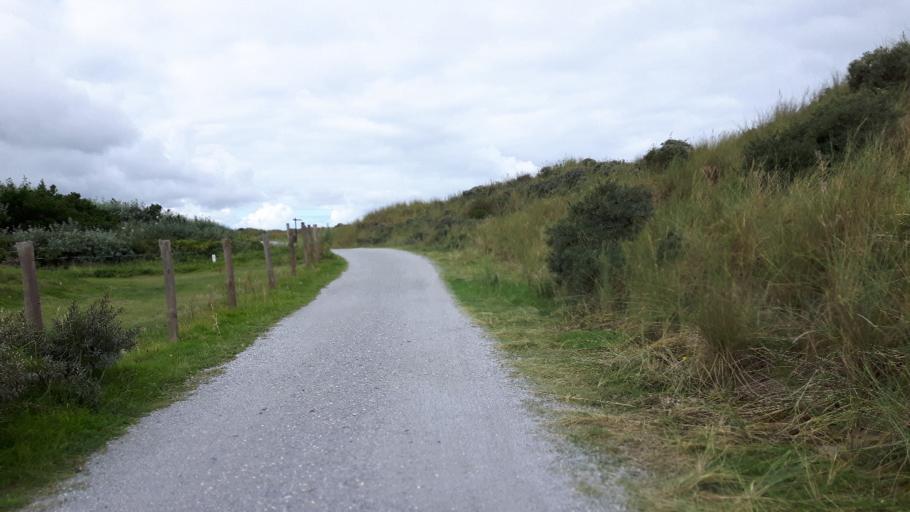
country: NL
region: Friesland
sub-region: Gemeente Ameland
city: Nes
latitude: 53.4579
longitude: 5.7654
